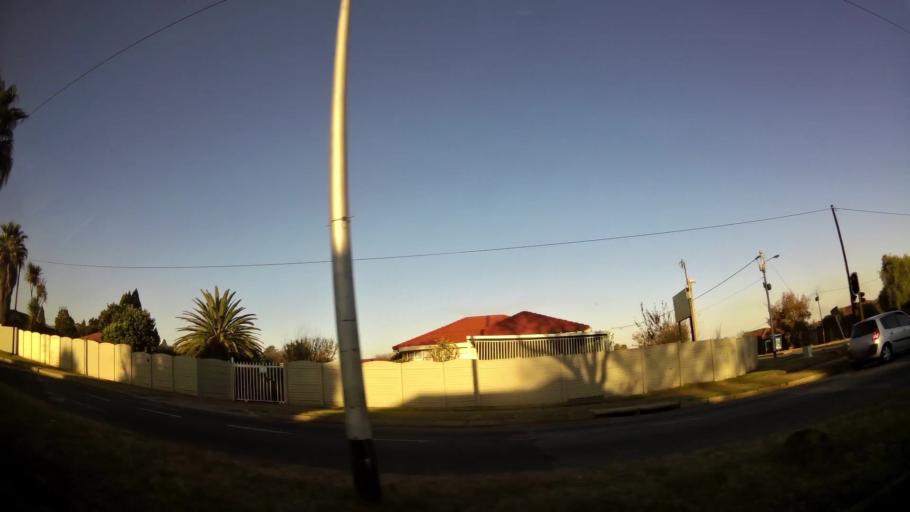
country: ZA
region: Gauteng
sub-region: City of Johannesburg Metropolitan Municipality
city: Roodepoort
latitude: -26.1549
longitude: 27.8769
